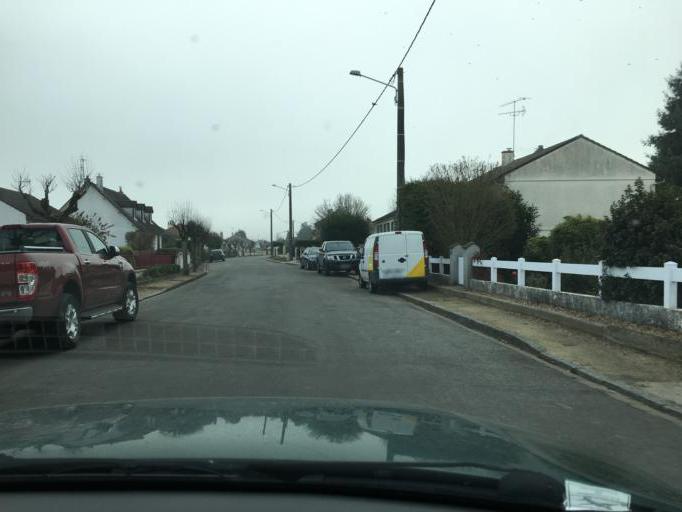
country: FR
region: Centre
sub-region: Departement du Loiret
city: Gidy
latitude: 47.9871
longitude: 1.8403
